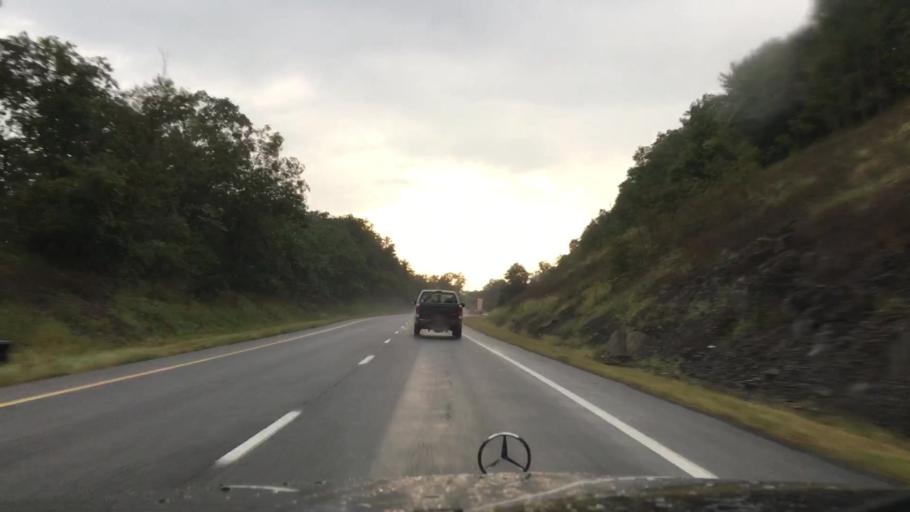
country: US
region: Virginia
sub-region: Frederick County
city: Shawnee Land
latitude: 39.3040
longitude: -78.2820
